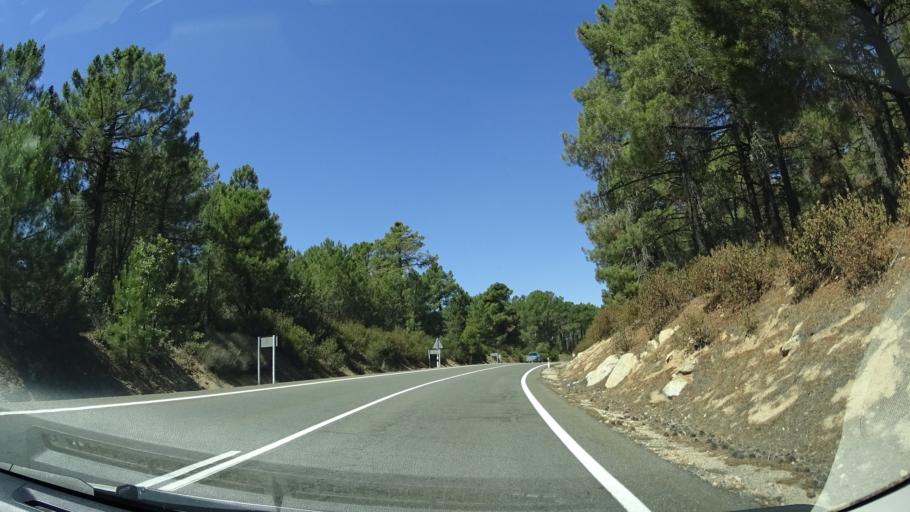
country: ES
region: Castille and Leon
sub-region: Provincia de Avila
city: Navalperal de Pinares
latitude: 40.5913
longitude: -4.3765
